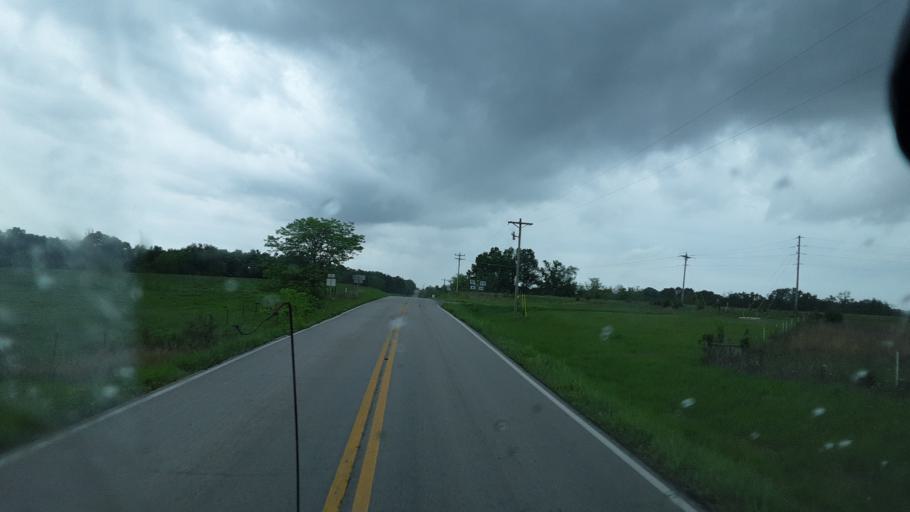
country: US
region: Missouri
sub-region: Monroe County
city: Paris
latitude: 39.4322
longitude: -92.2090
